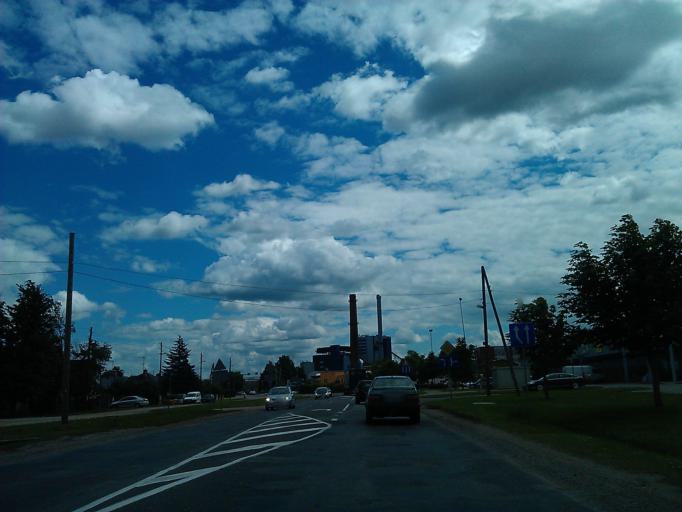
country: LV
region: Jelgava
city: Jelgava
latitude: 56.6378
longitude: 23.7040
